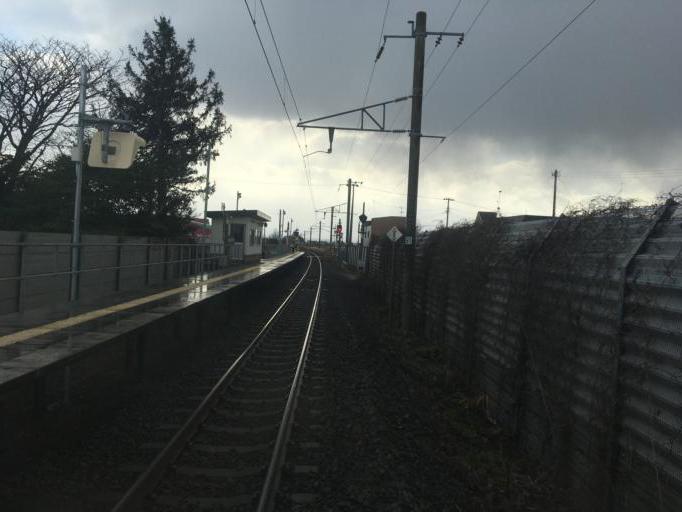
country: JP
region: Aomori
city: Aomori Shi
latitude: 40.8872
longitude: 140.6743
